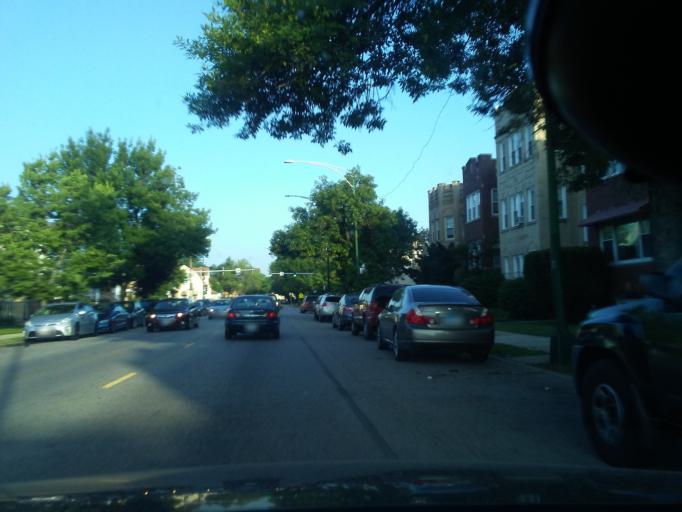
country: US
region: Illinois
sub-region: Cook County
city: Lincolnwood
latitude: 41.9752
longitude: -87.7616
